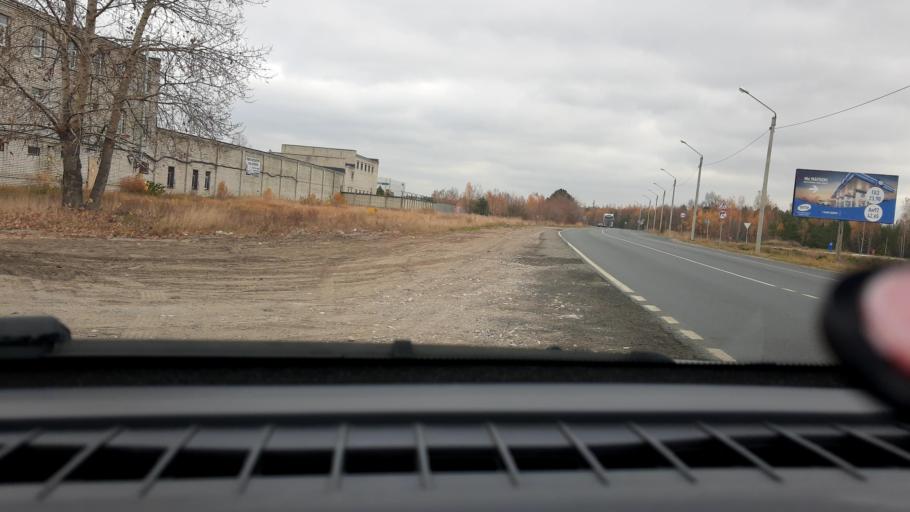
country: RU
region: Nizjnij Novgorod
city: Babino
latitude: 56.2600
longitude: 43.6590
